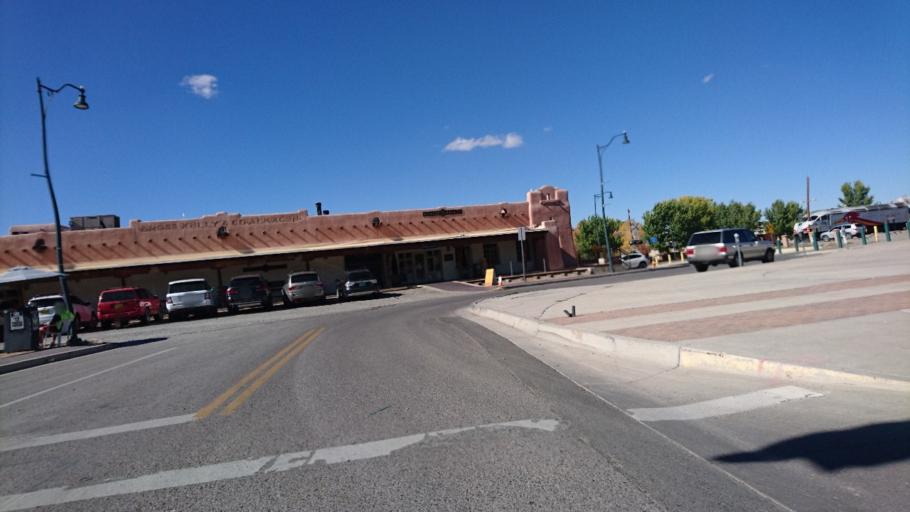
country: US
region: New Mexico
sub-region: Santa Fe County
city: Santa Fe
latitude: 35.6833
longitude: -105.9471
